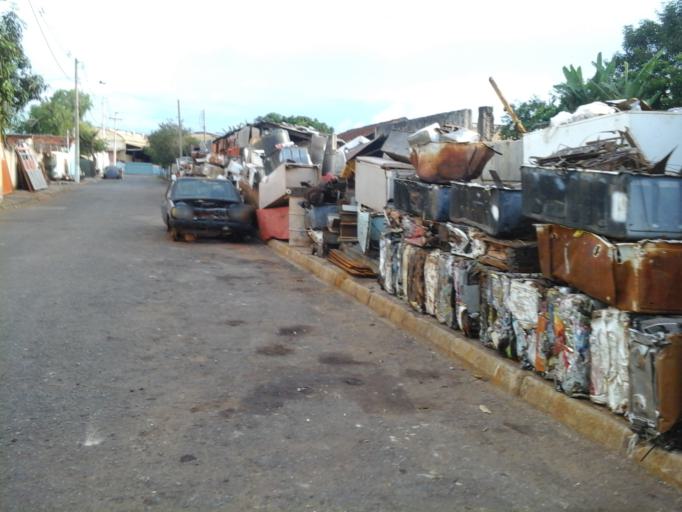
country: BR
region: Minas Gerais
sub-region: Patos De Minas
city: Patos de Minas
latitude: -18.5889
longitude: -46.5261
